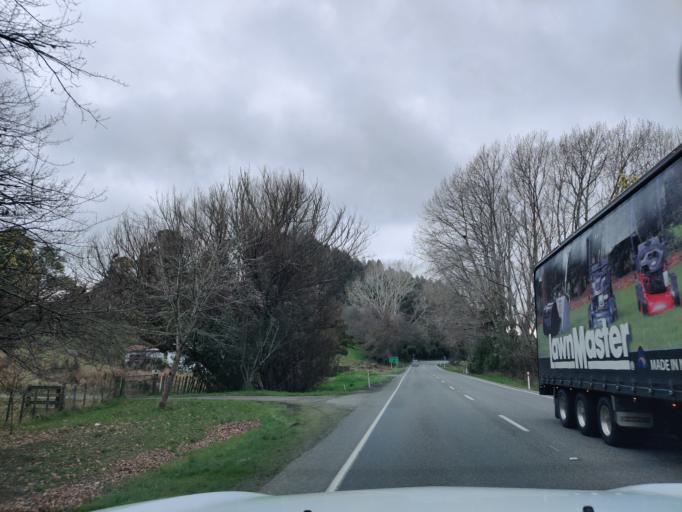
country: NZ
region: Manawatu-Wanganui
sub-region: Rangitikei District
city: Bulls
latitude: -39.9349
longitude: 175.5705
